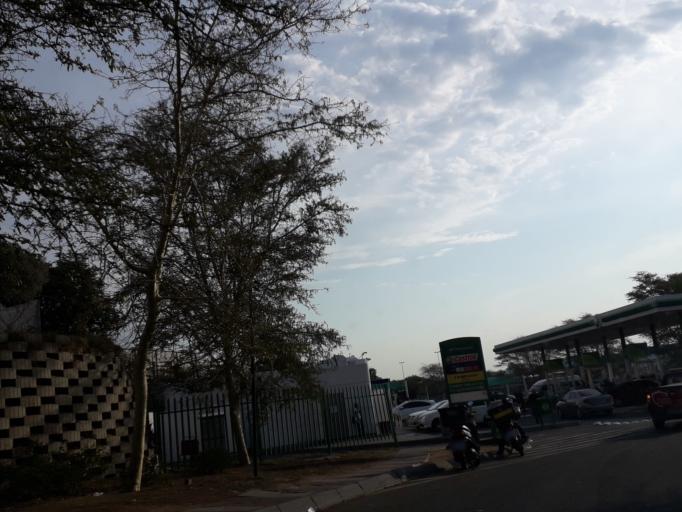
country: ZA
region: Gauteng
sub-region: City of Johannesburg Metropolitan Municipality
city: Diepsloot
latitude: -26.0164
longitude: 28.0110
